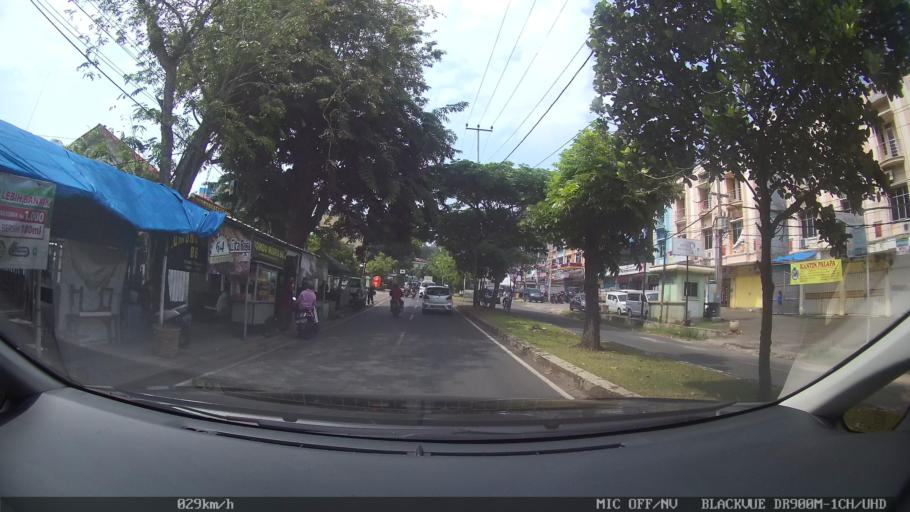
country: ID
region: Lampung
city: Bandarlampung
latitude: -5.4195
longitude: 105.2468
